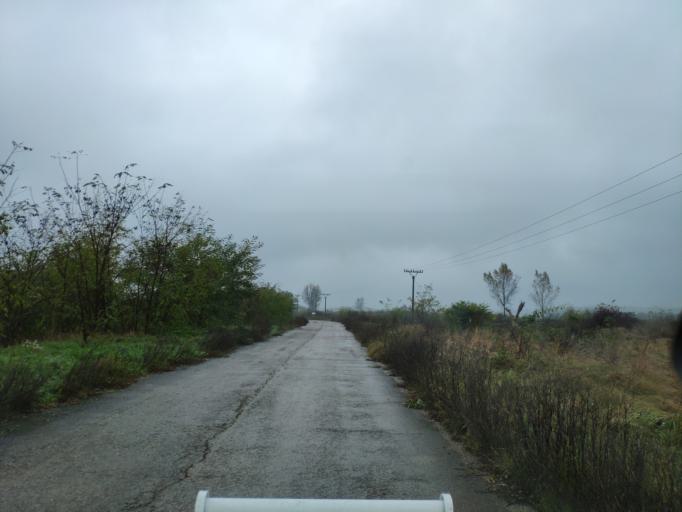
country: SK
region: Kosicky
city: Cierna nad Tisou
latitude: 48.4386
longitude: 22.0010
